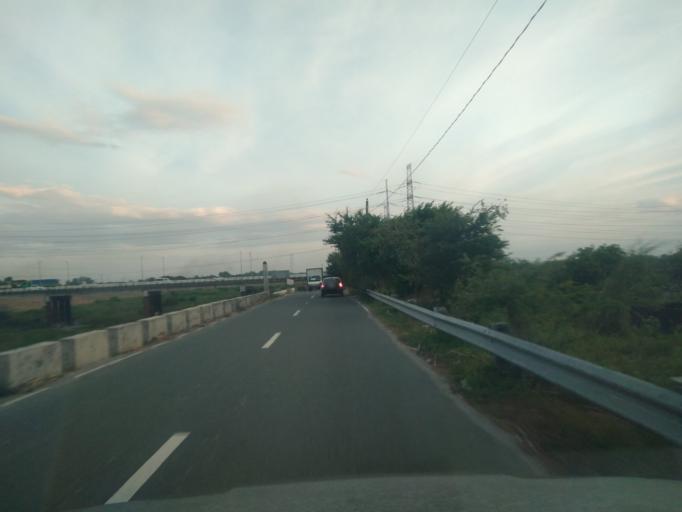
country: PH
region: Central Luzon
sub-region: Province of Pampanga
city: Bacolor
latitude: 14.9987
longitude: 120.6374
